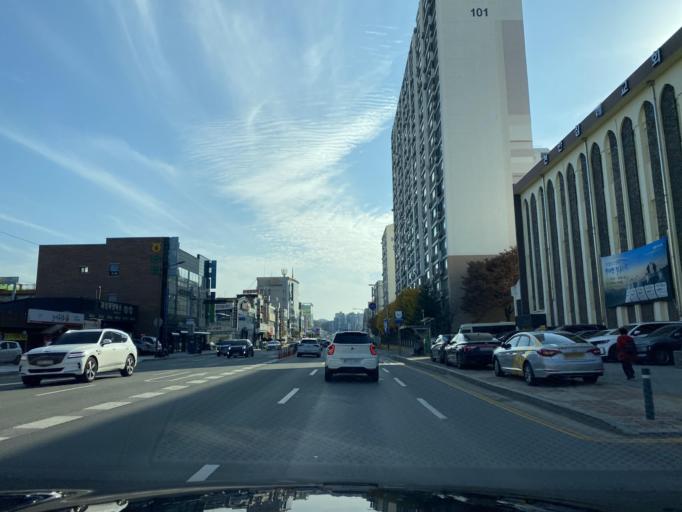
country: KR
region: Chungcheongnam-do
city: Cheonan
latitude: 36.8032
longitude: 127.1589
